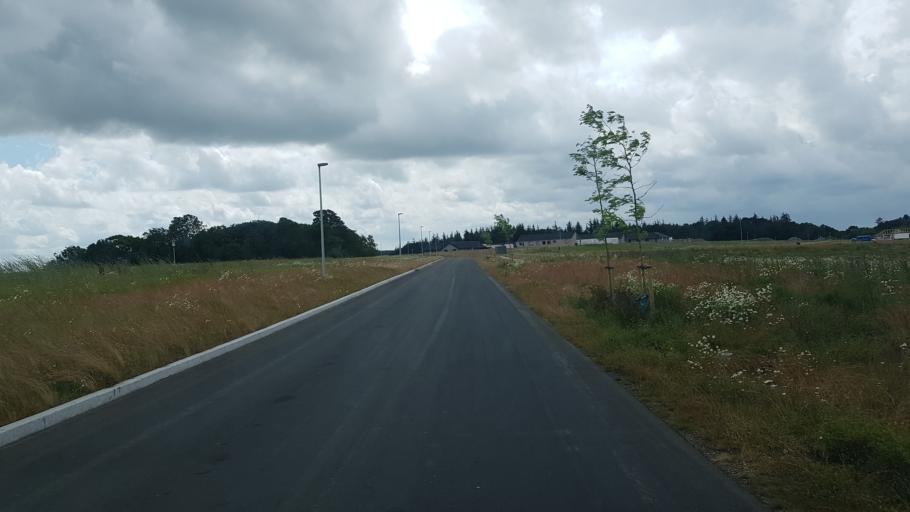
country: DK
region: South Denmark
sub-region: Kolding Kommune
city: Lunderskov
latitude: 55.4828
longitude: 9.2722
